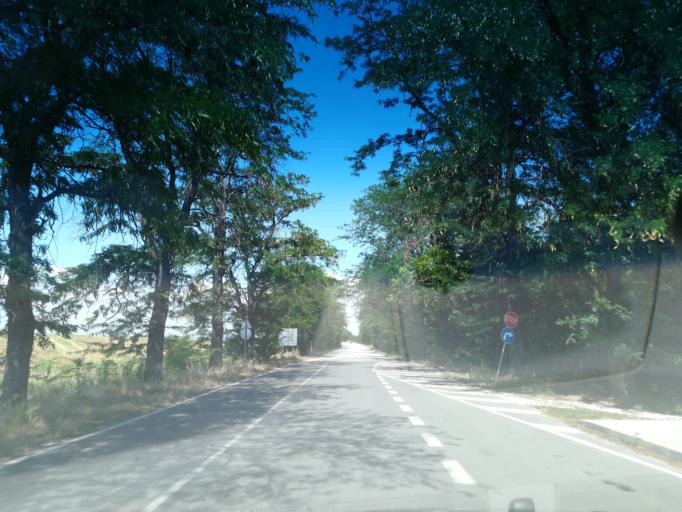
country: BG
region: Plovdiv
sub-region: Obshtina Sadovo
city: Sadovo
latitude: 42.0414
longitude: 25.1354
